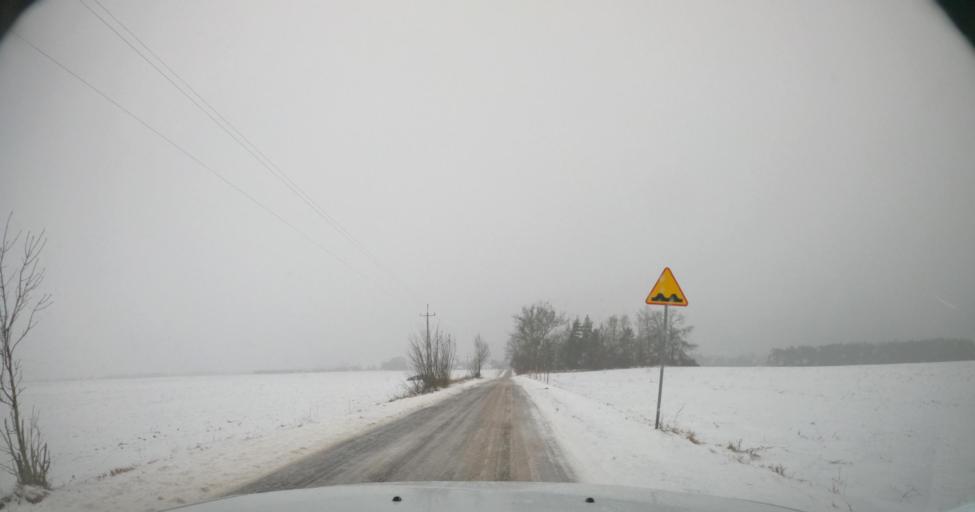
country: PL
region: West Pomeranian Voivodeship
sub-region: Powiat kamienski
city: Golczewo
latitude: 53.8042
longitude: 14.9669
